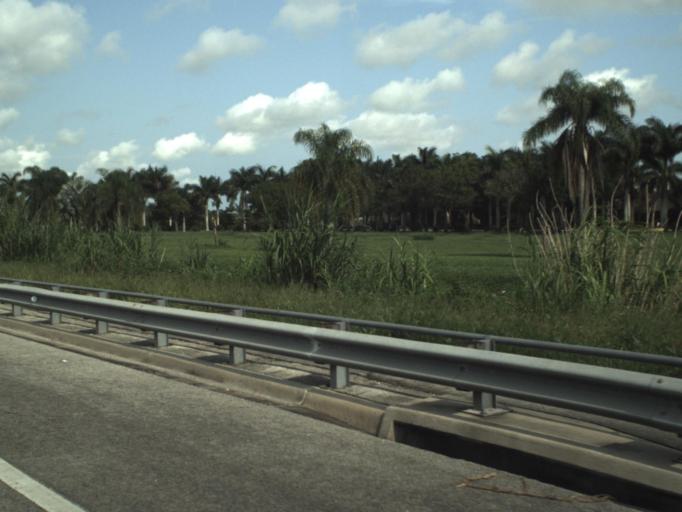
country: US
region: Florida
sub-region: Palm Beach County
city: Belle Glade Camp
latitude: 26.6639
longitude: -80.6758
